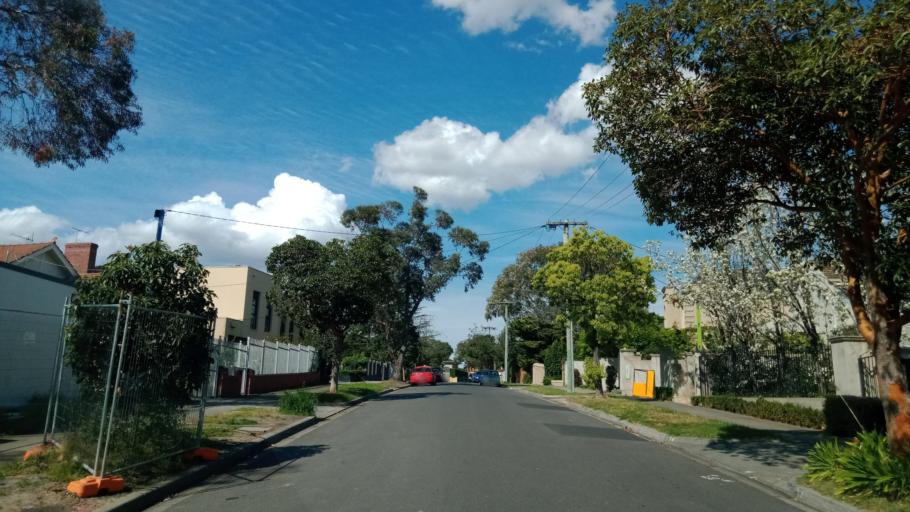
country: AU
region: Victoria
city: Glenferrie
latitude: -37.8443
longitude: 145.0471
